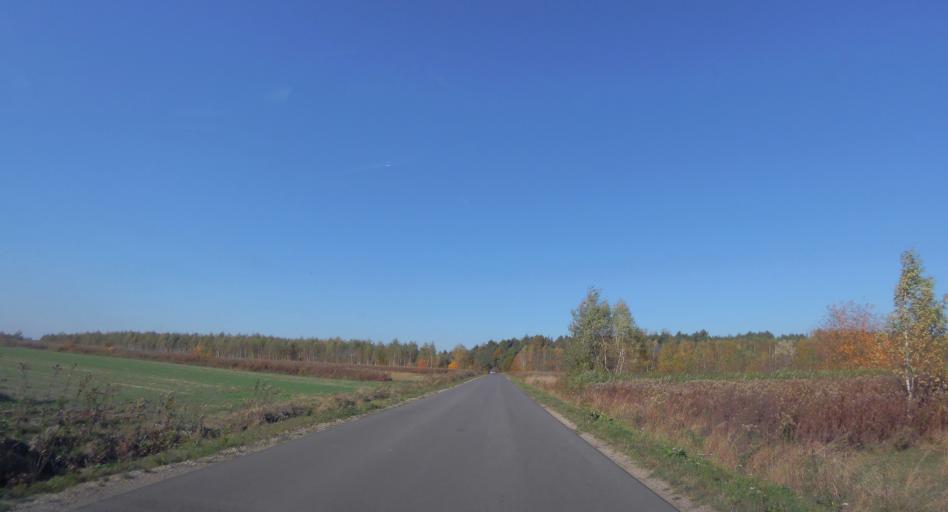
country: PL
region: Subcarpathian Voivodeship
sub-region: Powiat lezajski
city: Wola Zarczycka
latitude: 50.2874
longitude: 22.2686
